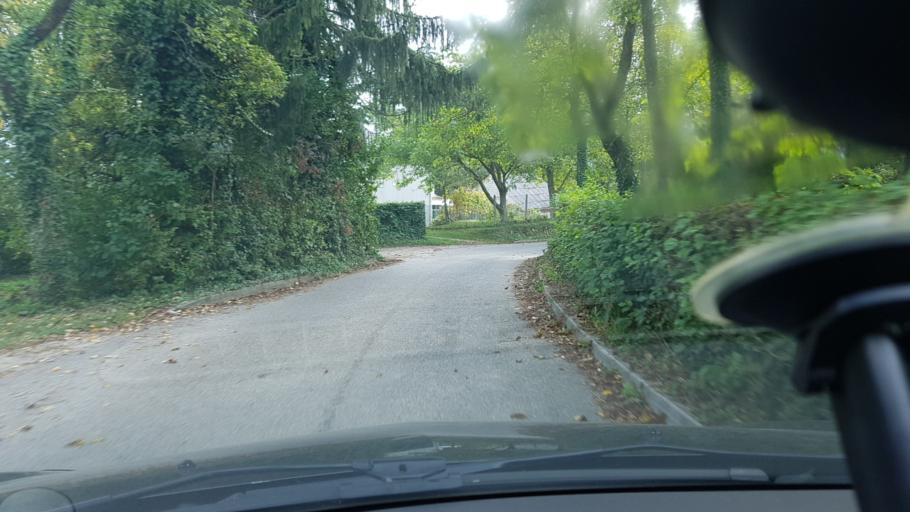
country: HR
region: Krapinsko-Zagorska
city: Radoboj
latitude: 46.1734
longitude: 15.9485
